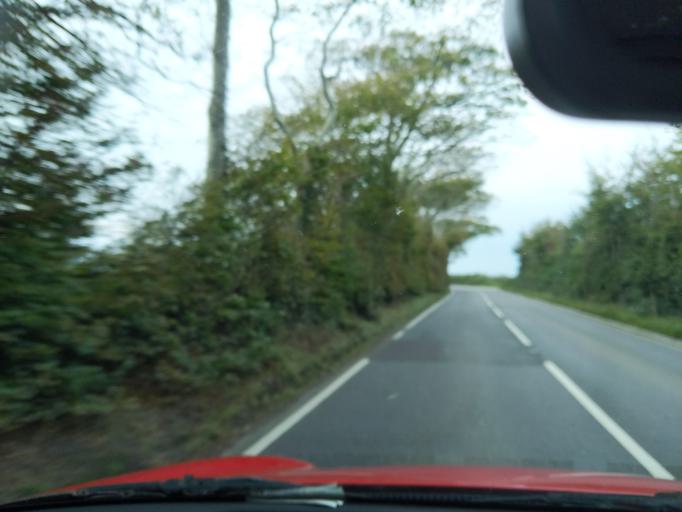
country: GB
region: England
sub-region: Devon
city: Okehampton
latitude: 50.7108
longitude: -4.0565
